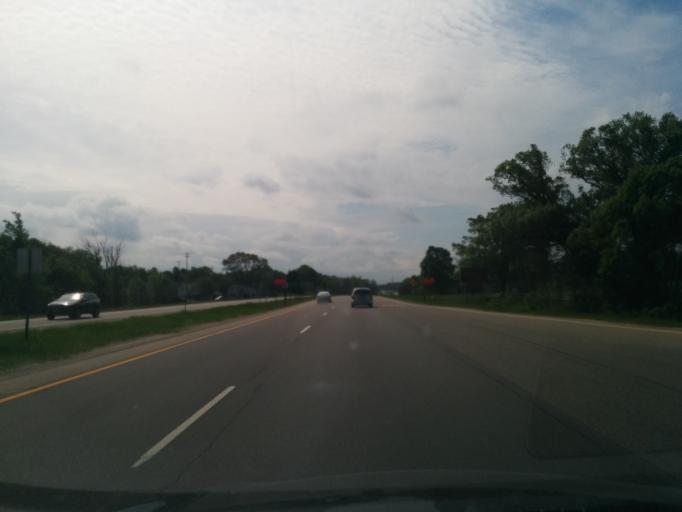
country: US
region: Michigan
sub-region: Ottawa County
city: Beechwood
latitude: 42.9229
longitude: -86.1483
